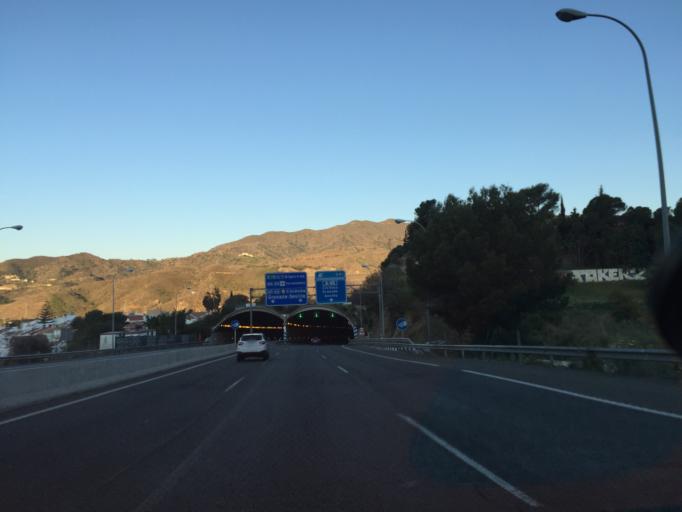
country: ES
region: Andalusia
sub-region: Provincia de Malaga
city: Malaga
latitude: 36.7566
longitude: -4.4195
